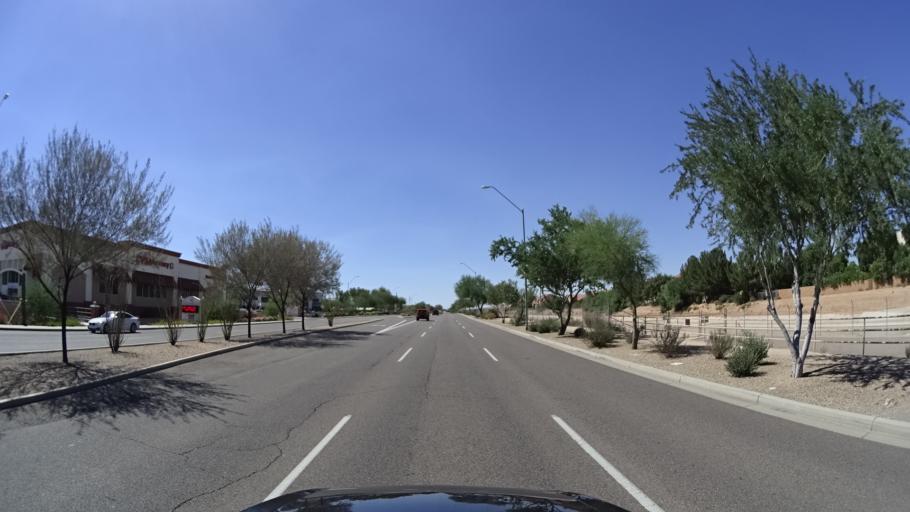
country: US
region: Arizona
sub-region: Maricopa County
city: Paradise Valley
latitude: 33.6384
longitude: -111.9267
